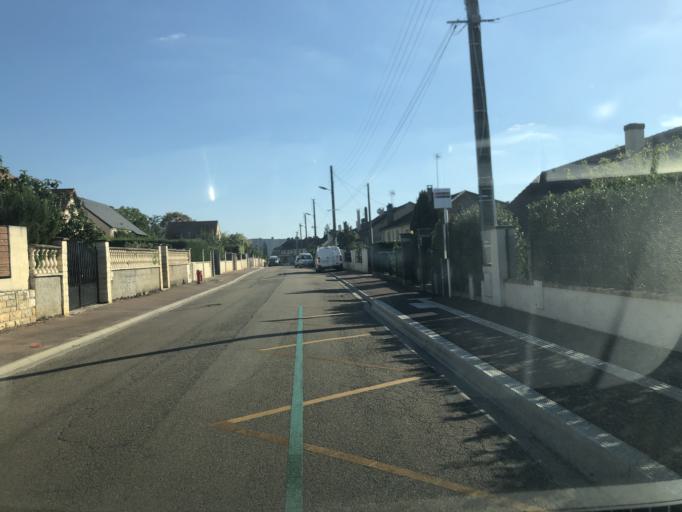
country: FR
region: Bourgogne
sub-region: Departement de l'Yonne
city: Auxerre
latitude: 47.7977
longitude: 3.5890
